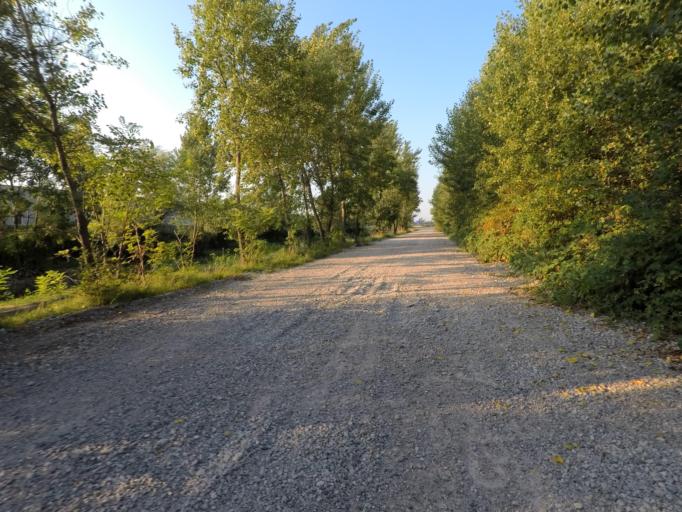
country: IT
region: Friuli Venezia Giulia
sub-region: Provincia di Udine
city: Trasaghis
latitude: 46.2836
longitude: 13.0994
